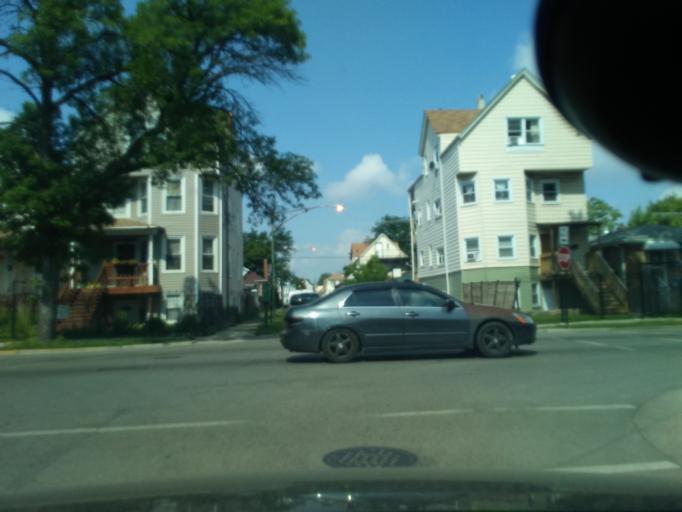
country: US
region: Illinois
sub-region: Cook County
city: Oak Park
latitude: 41.9187
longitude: -87.7558
